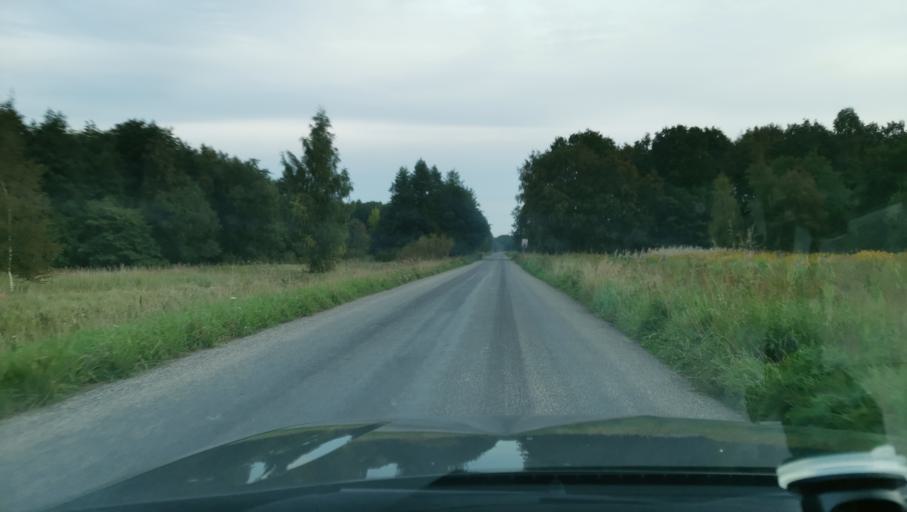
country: EE
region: Harju
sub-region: Saue vald
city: Laagri
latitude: 59.4235
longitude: 24.6247
